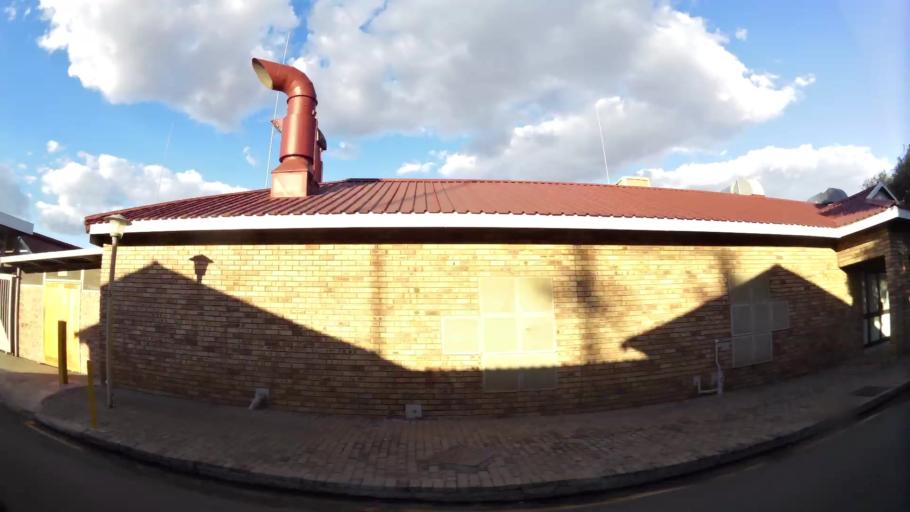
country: ZA
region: North-West
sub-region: Dr Kenneth Kaunda District Municipality
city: Potchefstroom
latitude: -26.6862
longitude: 27.0917
